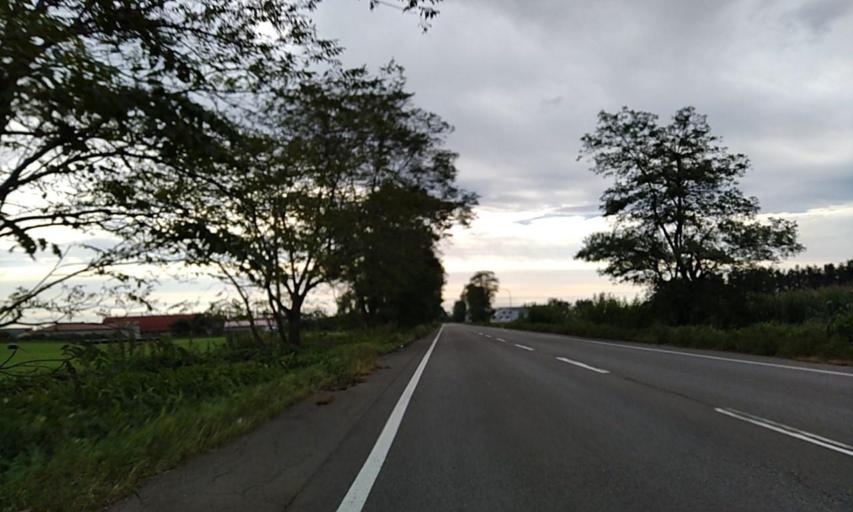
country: JP
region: Hokkaido
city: Obihiro
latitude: 42.9230
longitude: 142.9918
